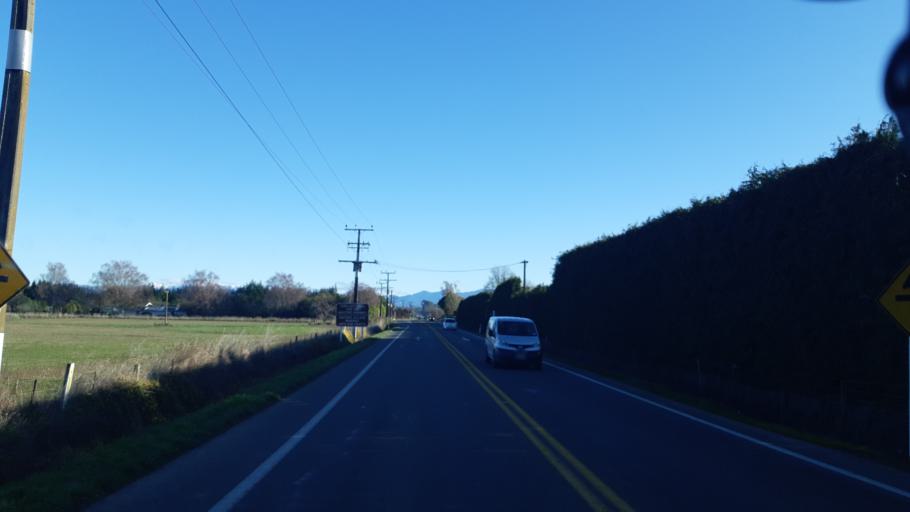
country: NZ
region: Tasman
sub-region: Tasman District
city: Mapua
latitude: -41.3075
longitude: 173.1245
